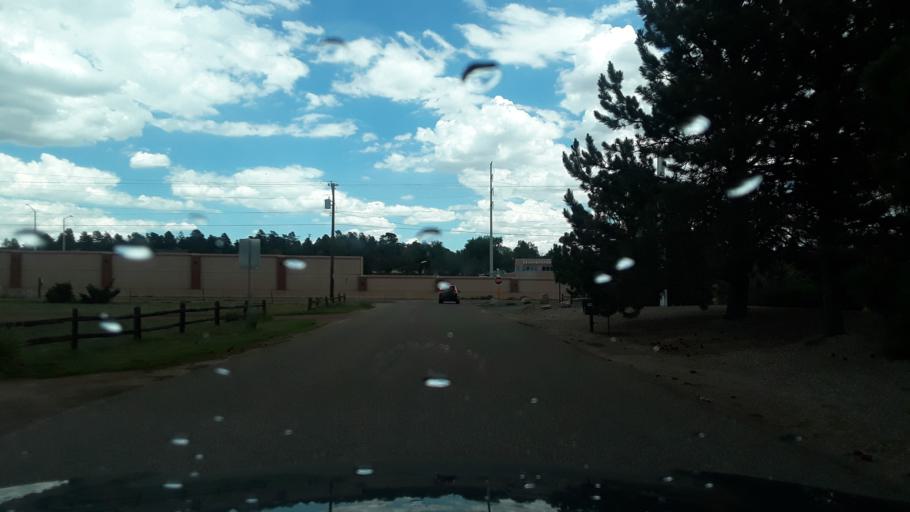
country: US
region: Colorado
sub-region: El Paso County
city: Air Force Academy
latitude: 38.9395
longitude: -104.8145
